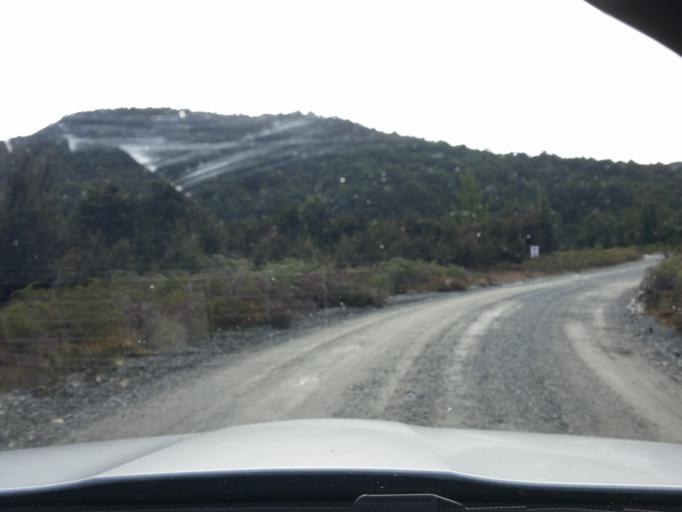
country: NZ
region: Southland
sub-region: Southland District
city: Te Anau
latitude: -45.4934
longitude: 167.6661
